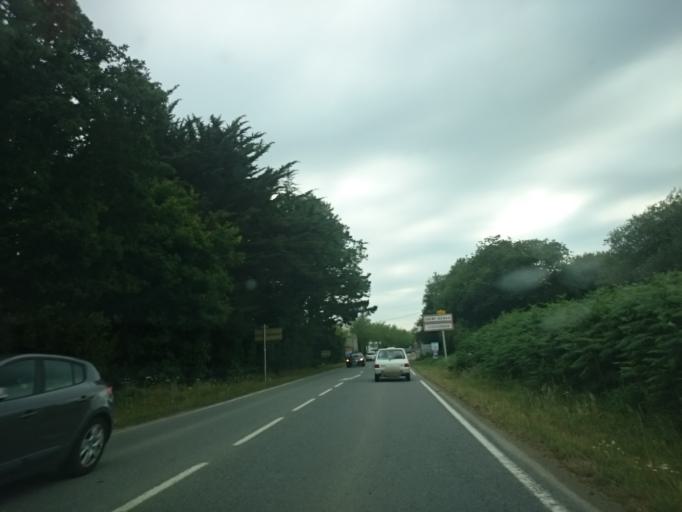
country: FR
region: Brittany
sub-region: Departement du Finistere
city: Saint-Renan
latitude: 48.4270
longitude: -4.6021
